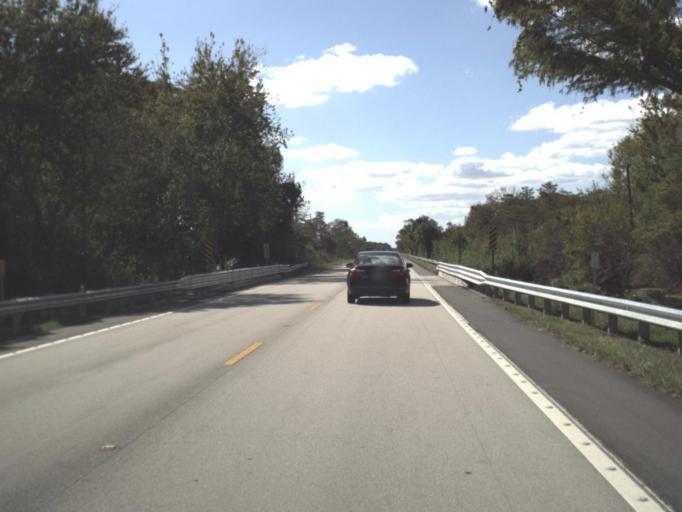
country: US
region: Florida
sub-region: Collier County
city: Marco
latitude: 25.8744
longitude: -81.2056
